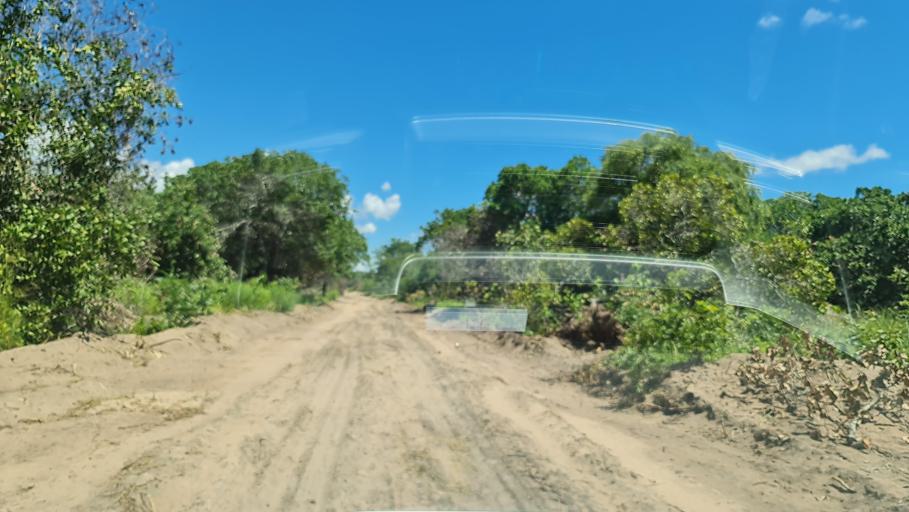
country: MZ
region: Nampula
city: Nampula
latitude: -15.3044
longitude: 39.8777
